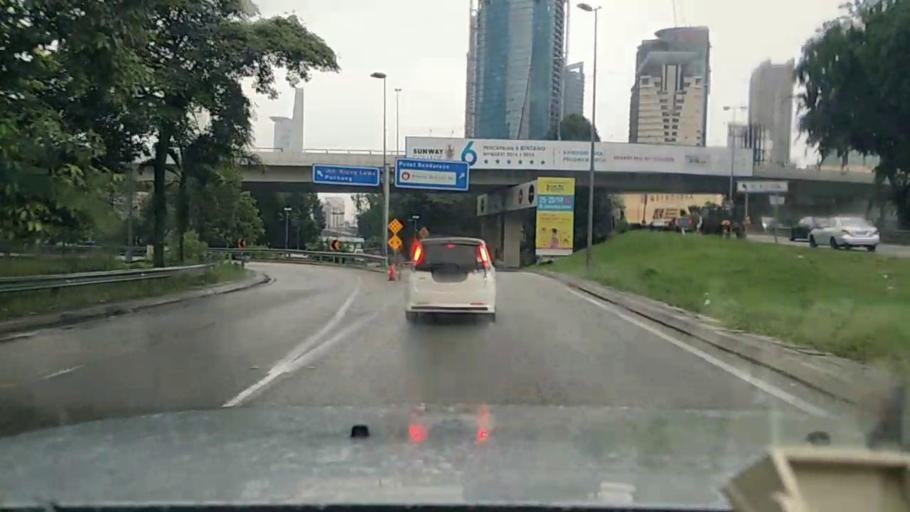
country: MY
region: Kuala Lumpur
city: Kuala Lumpur
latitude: 3.1141
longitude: 101.6798
